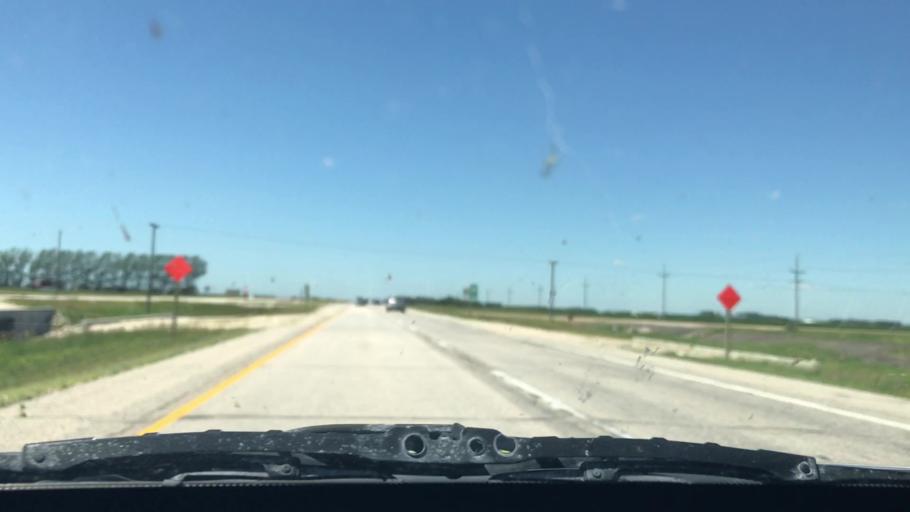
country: CA
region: Manitoba
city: Steinbach
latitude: 49.7330
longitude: -96.7257
